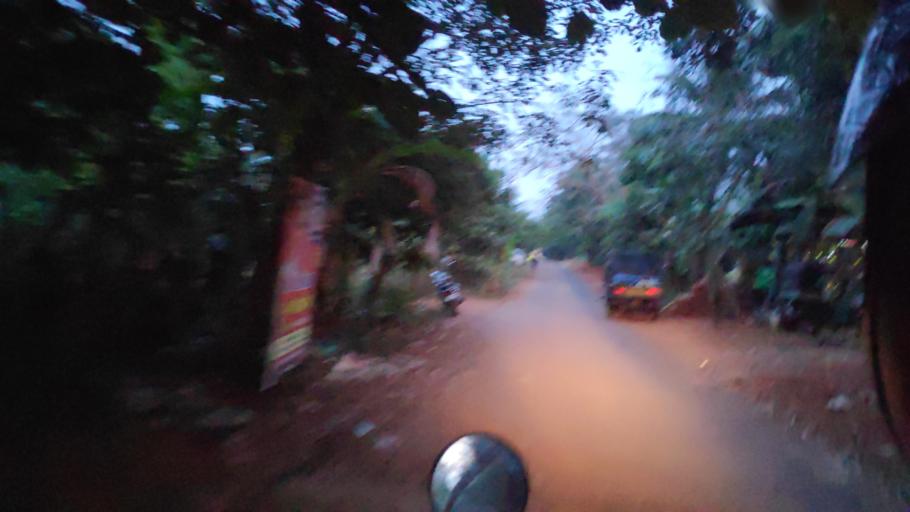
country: IN
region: Kerala
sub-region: Kozhikode
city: Kunnamangalam
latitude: 11.2805
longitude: 75.8304
